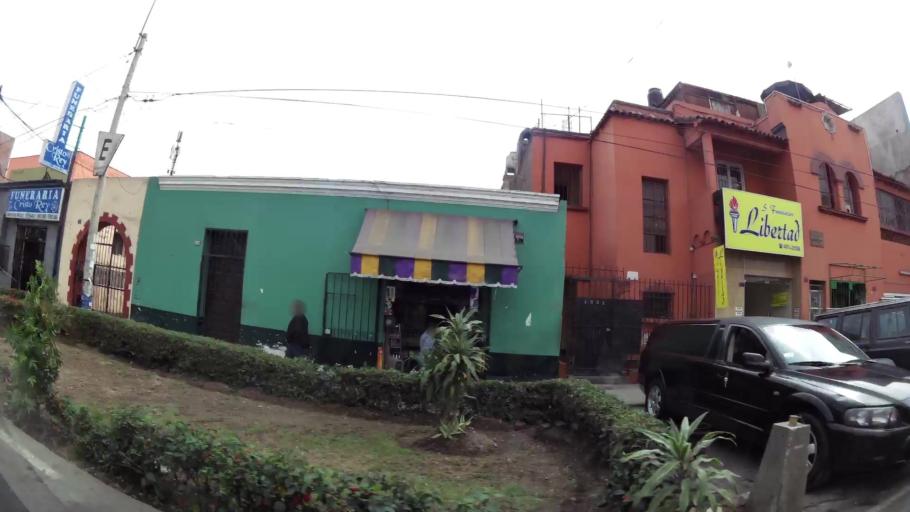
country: PE
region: Lima
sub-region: Lima
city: San Isidro
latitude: -12.0807
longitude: -77.0395
